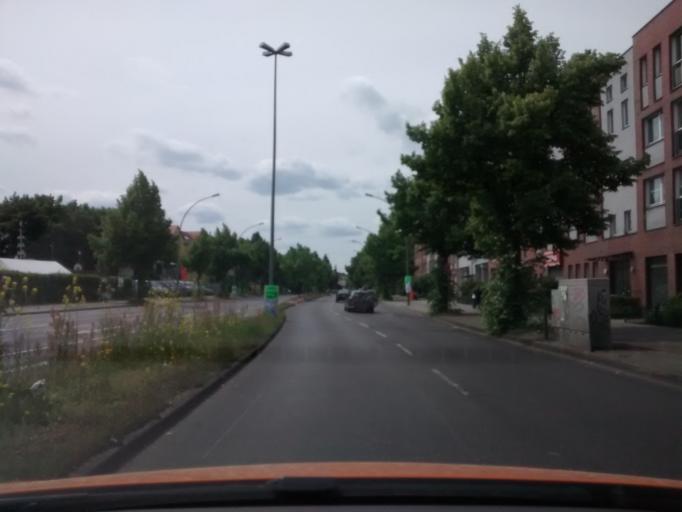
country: DE
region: Berlin
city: Marienfelde
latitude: 52.4123
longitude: 13.3613
